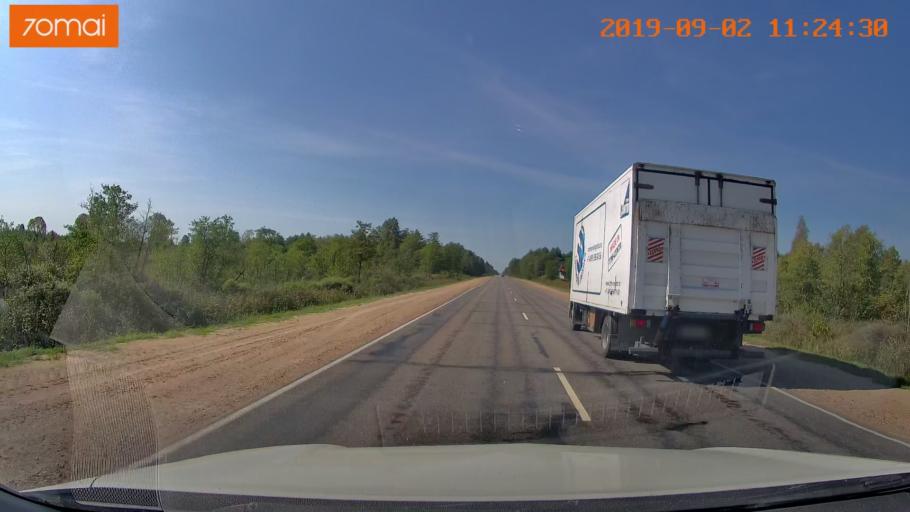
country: RU
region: Smolensk
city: Roslavl'
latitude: 54.0099
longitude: 32.9742
